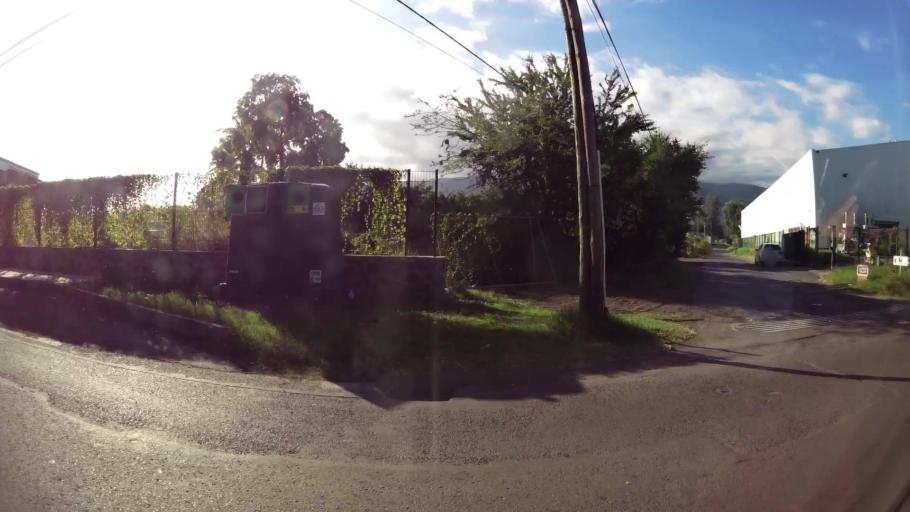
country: RE
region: Reunion
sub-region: Reunion
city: Saint-Louis
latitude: -21.2793
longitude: 55.3756
